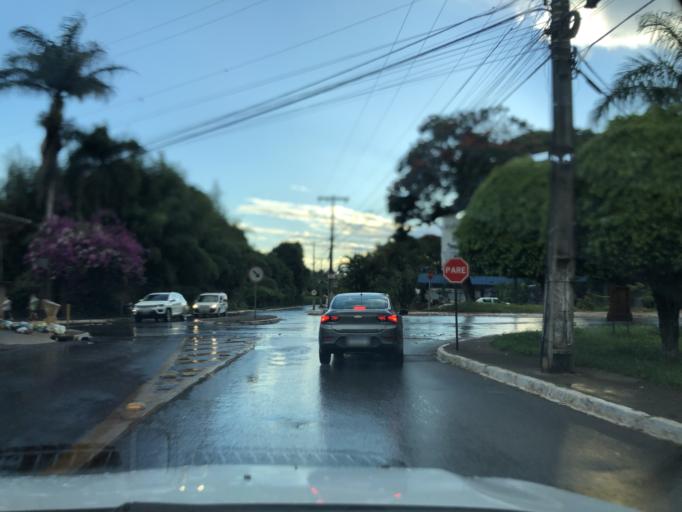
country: BR
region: Federal District
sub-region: Brasilia
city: Brasilia
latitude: -15.8723
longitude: -47.9648
